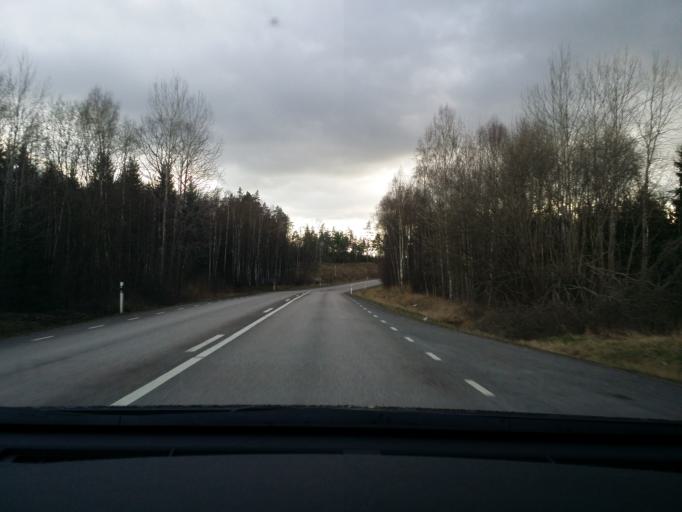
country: SE
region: Soedermanland
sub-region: Eskilstuna Kommun
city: Eskilstuna
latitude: 59.3857
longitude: 16.6224
